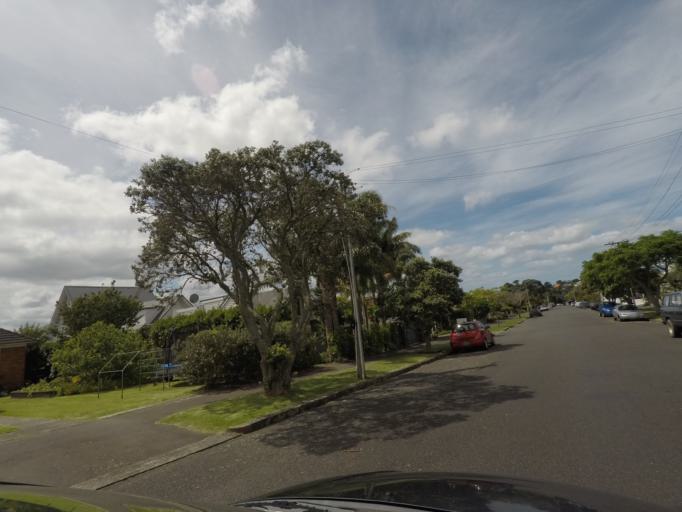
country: NZ
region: Auckland
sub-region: Auckland
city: Auckland
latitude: -36.8525
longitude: 174.7178
